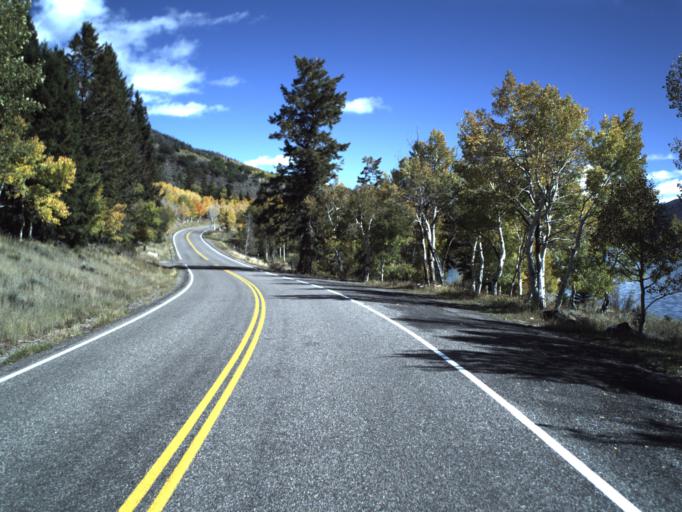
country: US
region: Utah
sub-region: Wayne County
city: Loa
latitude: 38.5415
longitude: -111.7320
